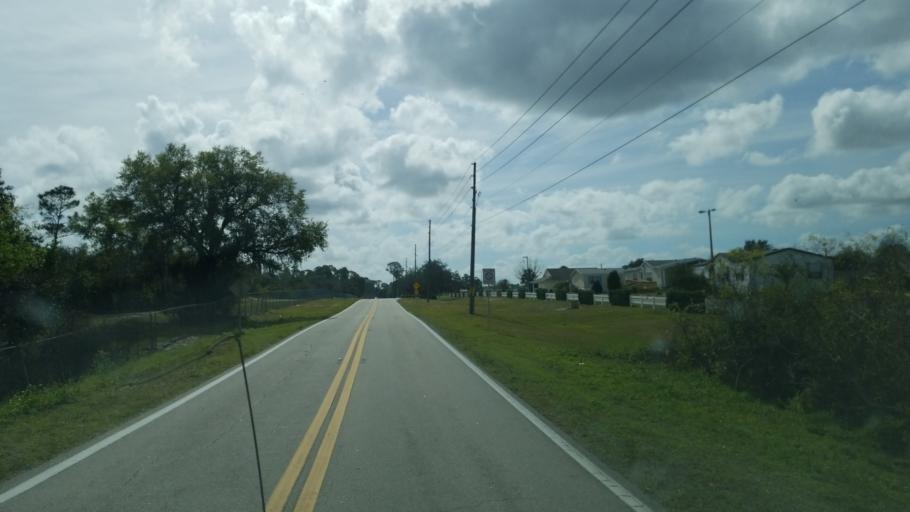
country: US
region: Florida
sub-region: Polk County
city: Dundee
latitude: 28.0041
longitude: -81.5256
